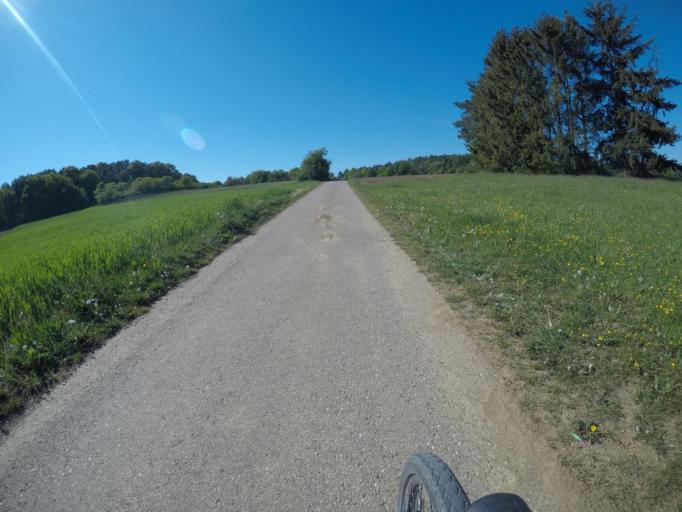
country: DE
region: Baden-Wuerttemberg
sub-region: Karlsruhe Region
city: Friolzheim
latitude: 48.8223
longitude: 8.8517
